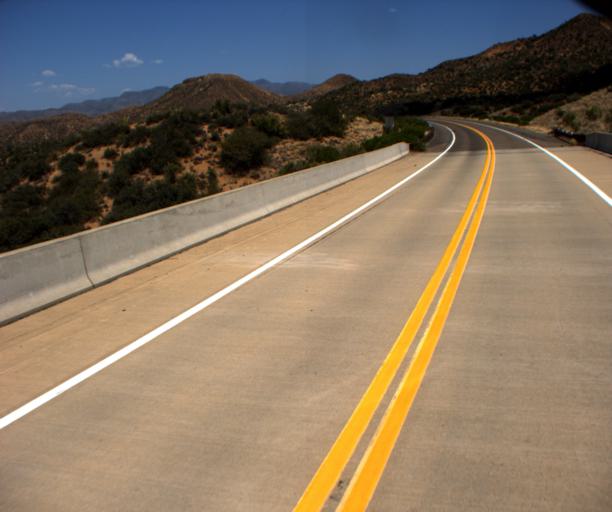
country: US
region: Arizona
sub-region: Gila County
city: Claypool
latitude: 33.5246
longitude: -110.9095
